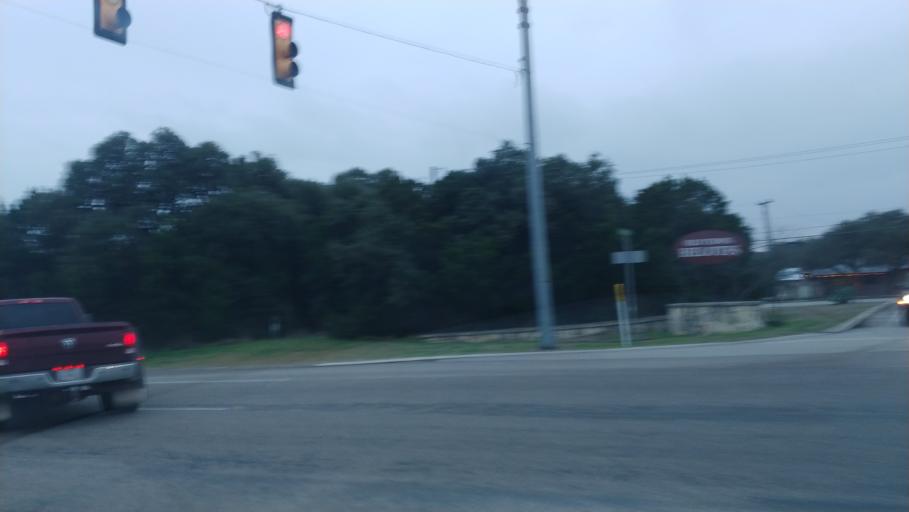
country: US
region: Texas
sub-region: Bexar County
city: Helotes
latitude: 29.5813
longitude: -98.6922
